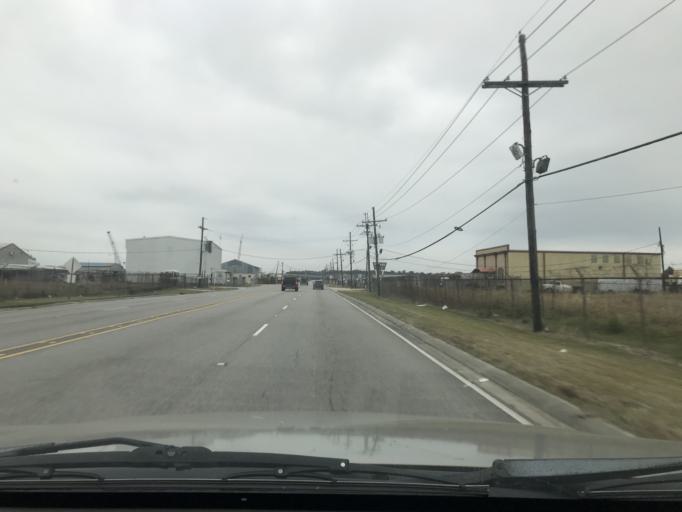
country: US
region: Louisiana
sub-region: Jefferson Parish
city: Woodmere
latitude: 29.8792
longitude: -90.0750
